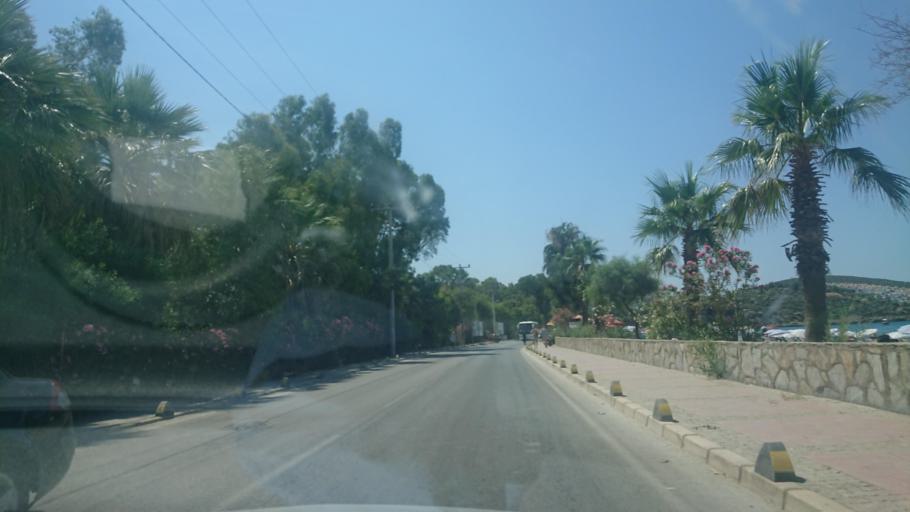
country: TR
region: Aydin
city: Kusadasi
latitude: 37.9027
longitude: 27.2727
